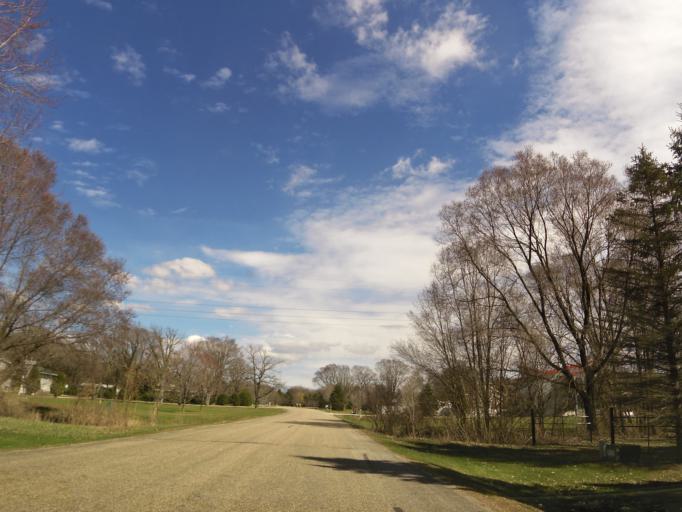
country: US
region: Minnesota
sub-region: Olmsted County
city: Rochester
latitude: 44.0058
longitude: -92.3716
